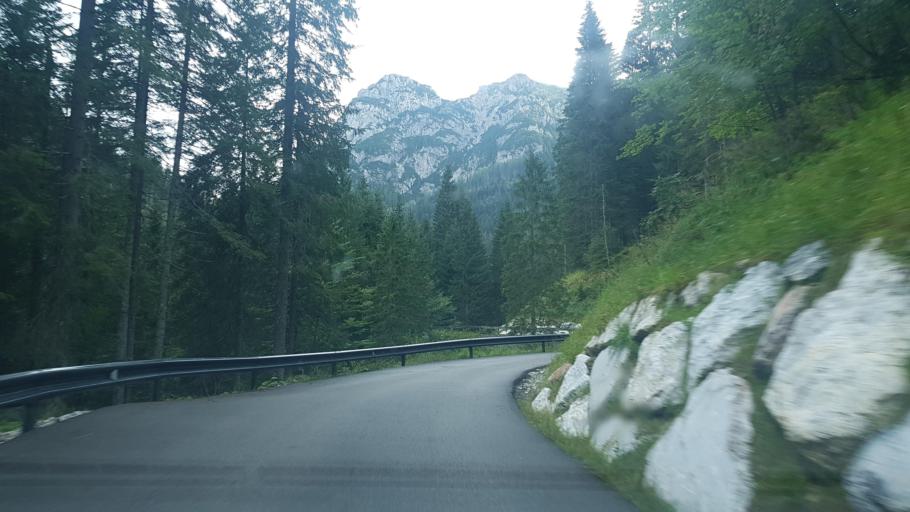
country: IT
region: Veneto
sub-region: Provincia di Belluno
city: Granvilla
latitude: 46.5779
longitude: 12.7251
